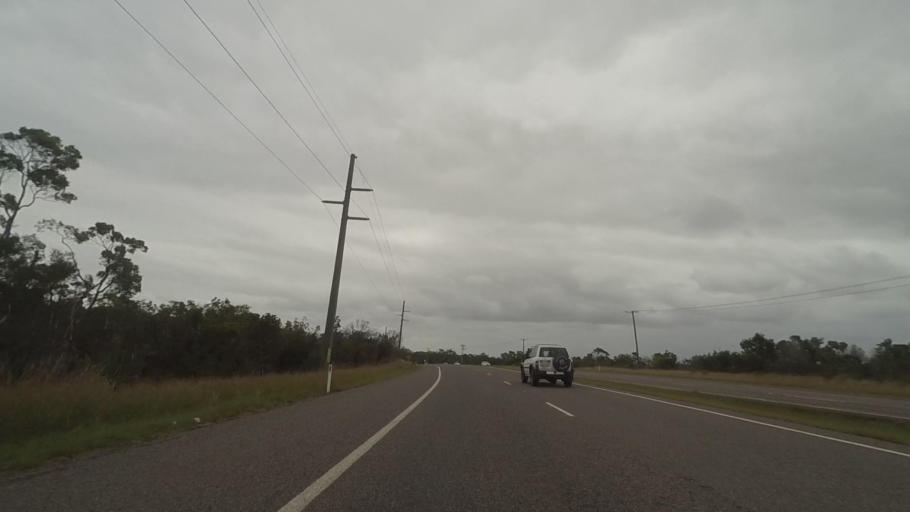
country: AU
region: New South Wales
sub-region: Wyong Shire
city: Kingfisher Shores
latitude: -33.1855
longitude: 151.5870
